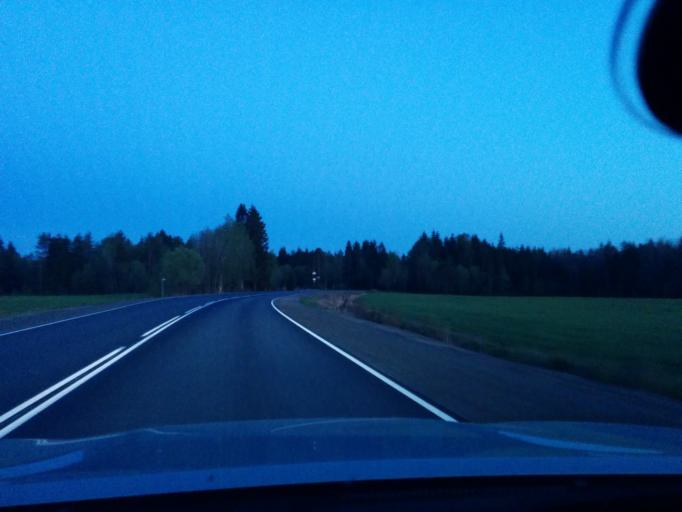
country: RU
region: Leningrad
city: Verkhniye Osel'ki
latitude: 60.2011
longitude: 30.4266
